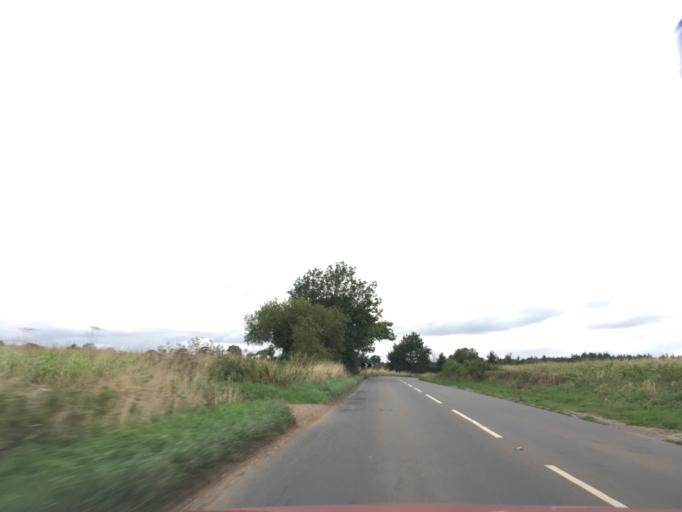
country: GB
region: England
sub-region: Wiltshire
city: Calne
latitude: 51.3922
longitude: -2.0422
